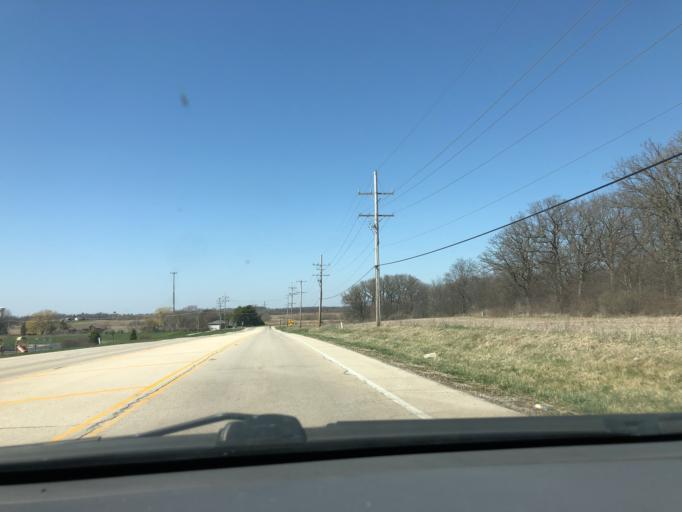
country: US
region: Illinois
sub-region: Kane County
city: Hampshire
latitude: 42.1201
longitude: -88.4912
